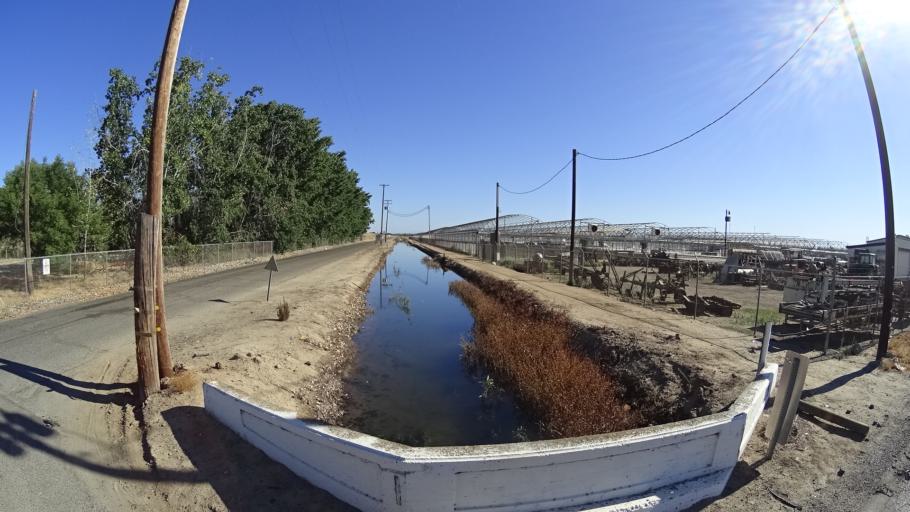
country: US
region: California
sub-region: Fresno County
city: West Park
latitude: 36.6922
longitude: -119.8268
